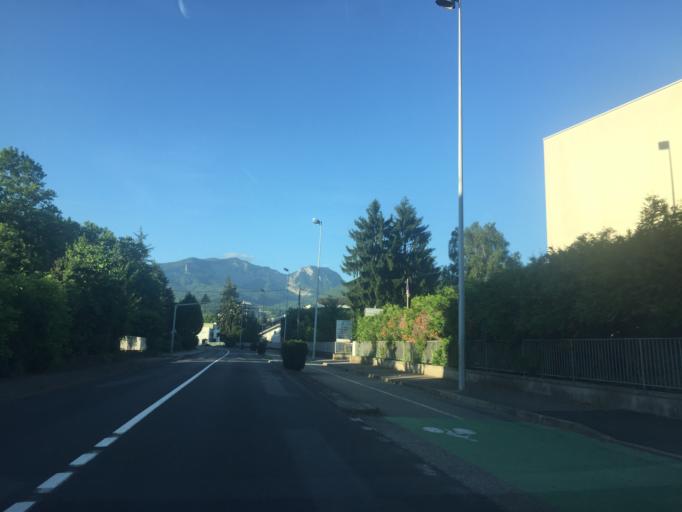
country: FR
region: Rhone-Alpes
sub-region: Departement de la Savoie
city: Cognin
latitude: 45.5646
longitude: 5.8934
